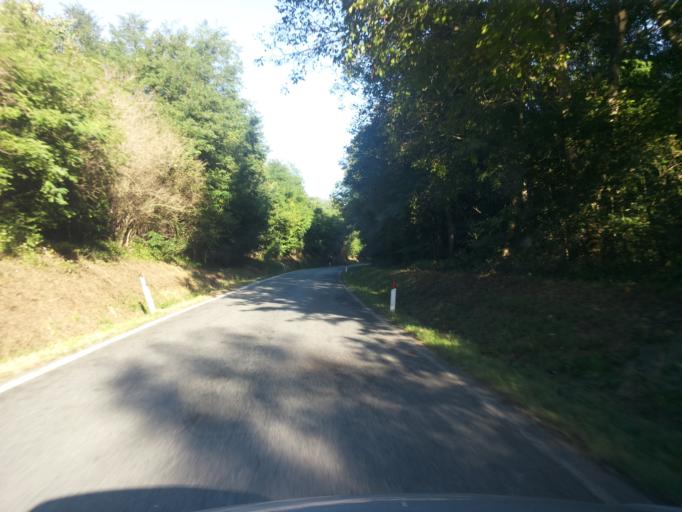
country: IT
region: Piedmont
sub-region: Provincia di Torino
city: Caravino
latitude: 45.3990
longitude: 7.9477
